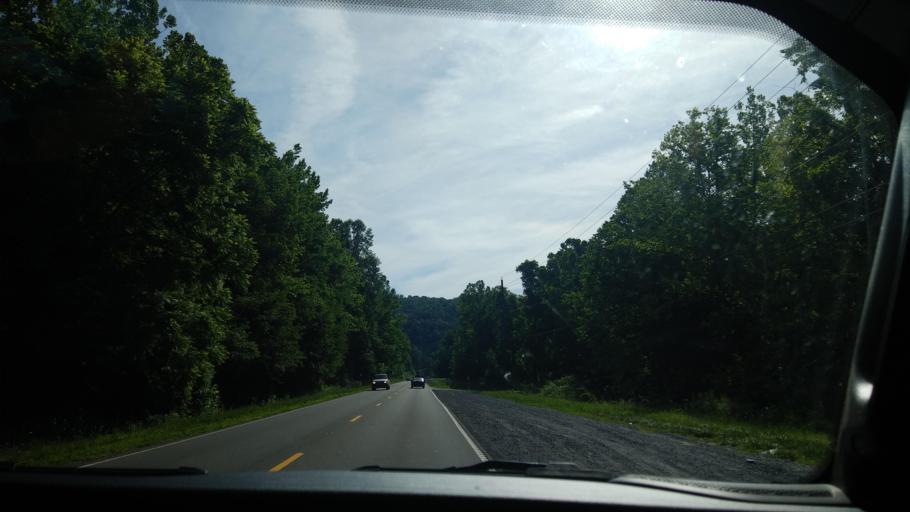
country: US
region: Tennessee
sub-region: Sevier County
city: Gatlinburg
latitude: 35.7598
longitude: -83.3785
